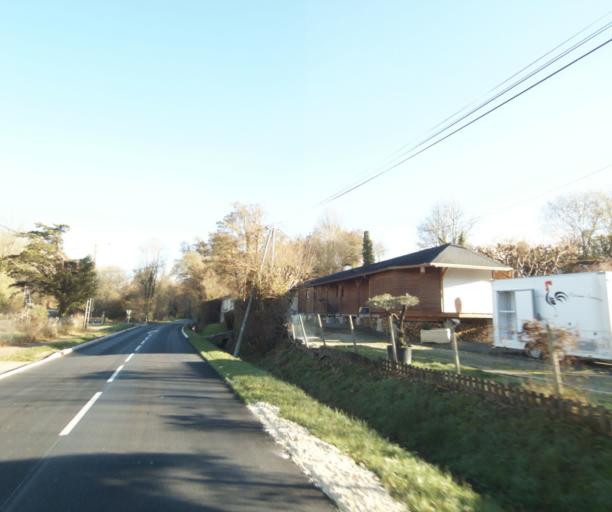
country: FR
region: Poitou-Charentes
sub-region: Departement de la Charente-Maritime
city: Fontcouverte
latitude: 45.7563
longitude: -0.5633
